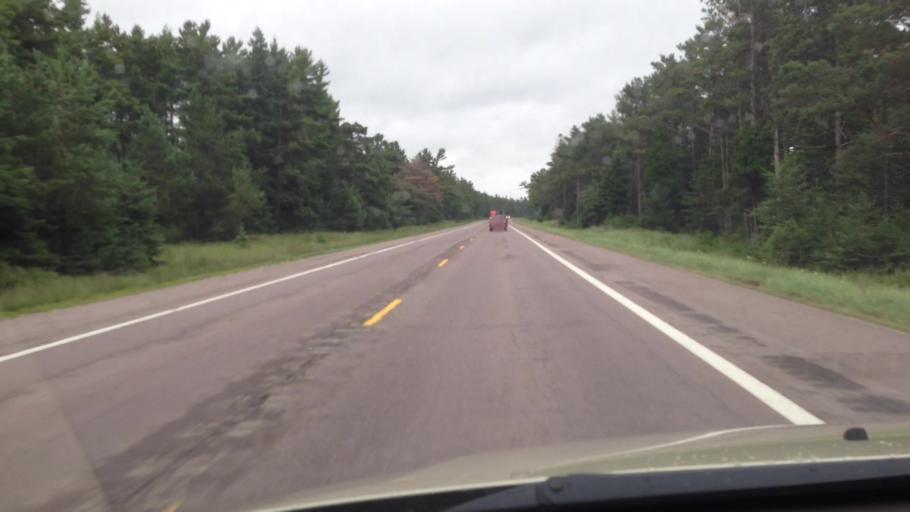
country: US
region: Michigan
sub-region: Schoolcraft County
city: Manistique
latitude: 45.9118
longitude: -86.3218
